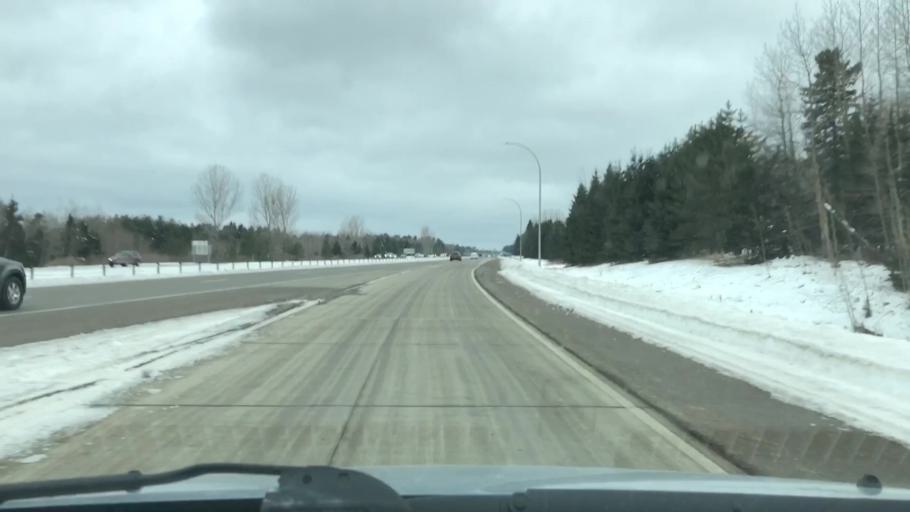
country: US
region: Minnesota
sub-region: Carlton County
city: Esko
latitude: 46.7028
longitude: -92.3063
